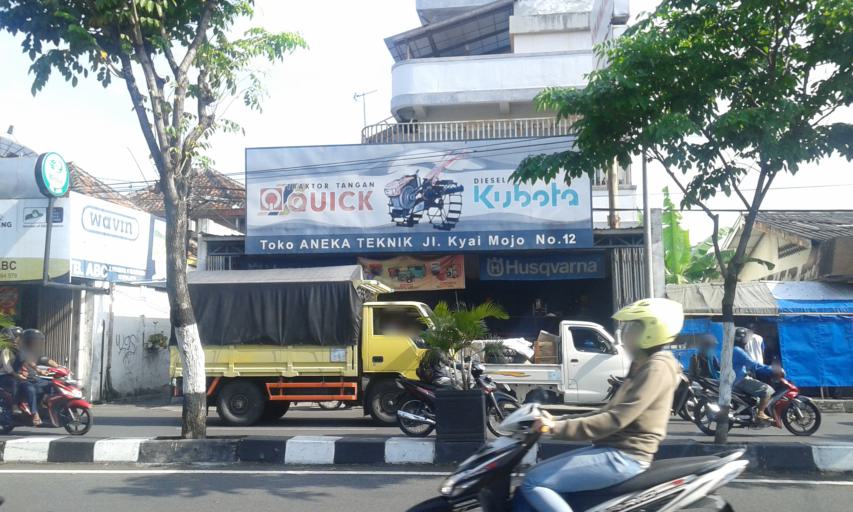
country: ID
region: Daerah Istimewa Yogyakarta
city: Yogyakarta
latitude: -7.7829
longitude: 110.3601
